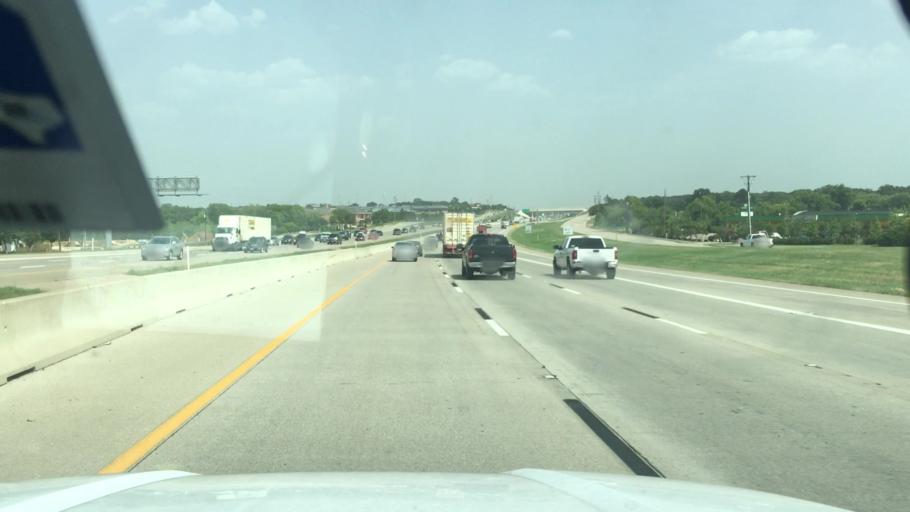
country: US
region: Texas
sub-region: Tarrant County
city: Southlake
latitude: 32.9587
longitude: -97.1448
